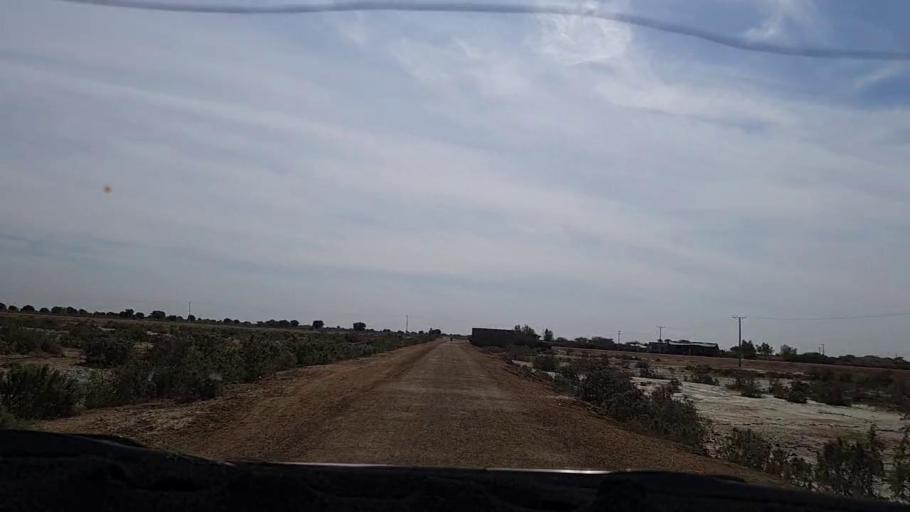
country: PK
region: Sindh
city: Pithoro
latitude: 25.4927
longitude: 69.4564
